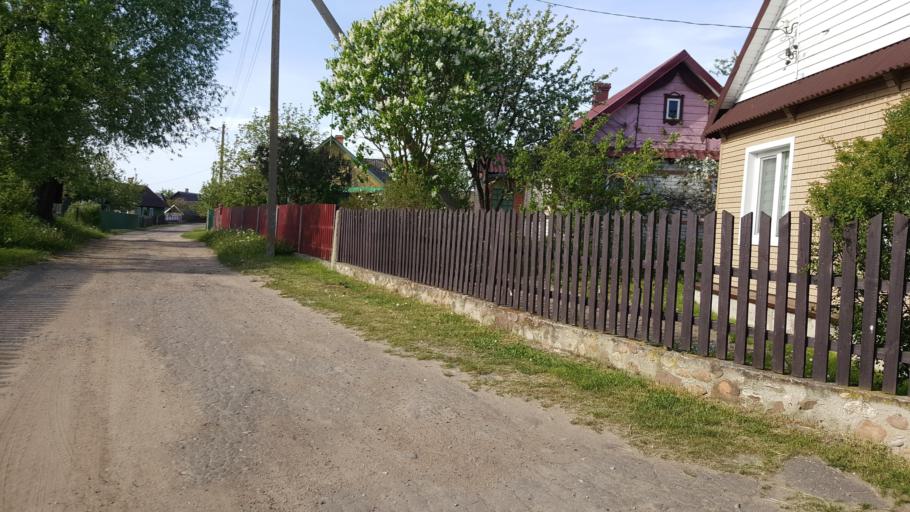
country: BY
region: Brest
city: Kamyanyets
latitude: 52.3663
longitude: 23.8783
